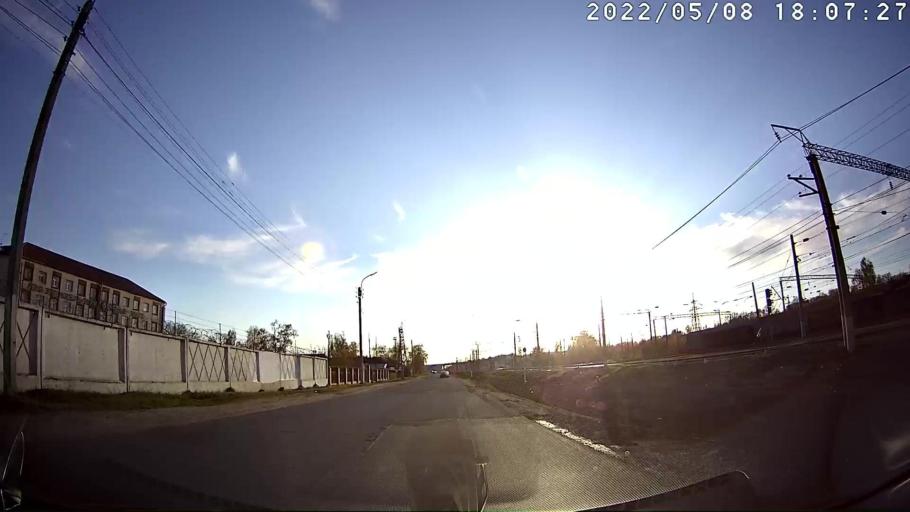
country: RU
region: Tatarstan
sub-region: Zelenodol'skiy Rayon
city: Zelenodolsk
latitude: 55.8413
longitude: 48.5561
